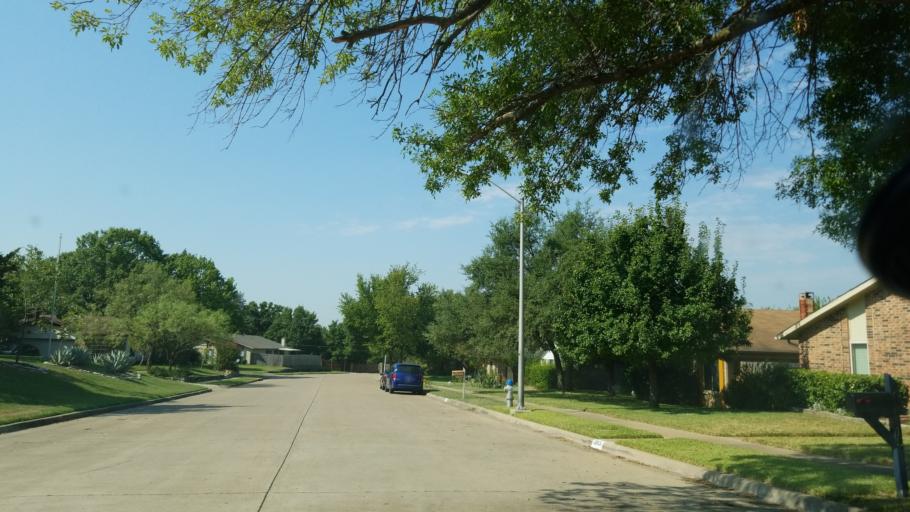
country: US
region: Texas
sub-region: Dallas County
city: Garland
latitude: 32.8729
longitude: -96.6963
